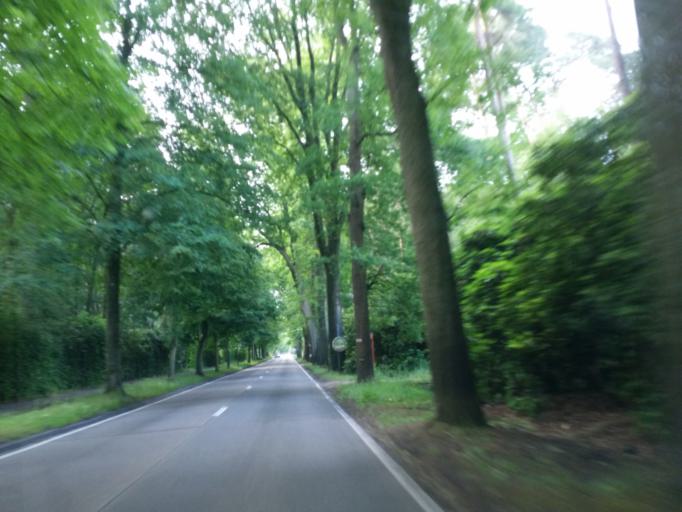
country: BE
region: Flanders
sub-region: Provincie Antwerpen
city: Brasschaat
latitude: 51.3121
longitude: 4.4785
